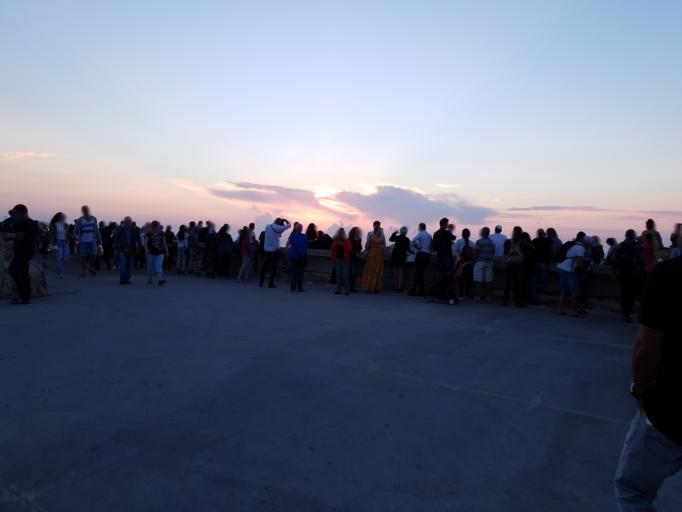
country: IL
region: Tel Aviv
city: Yafo
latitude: 32.0505
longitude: 34.7485
